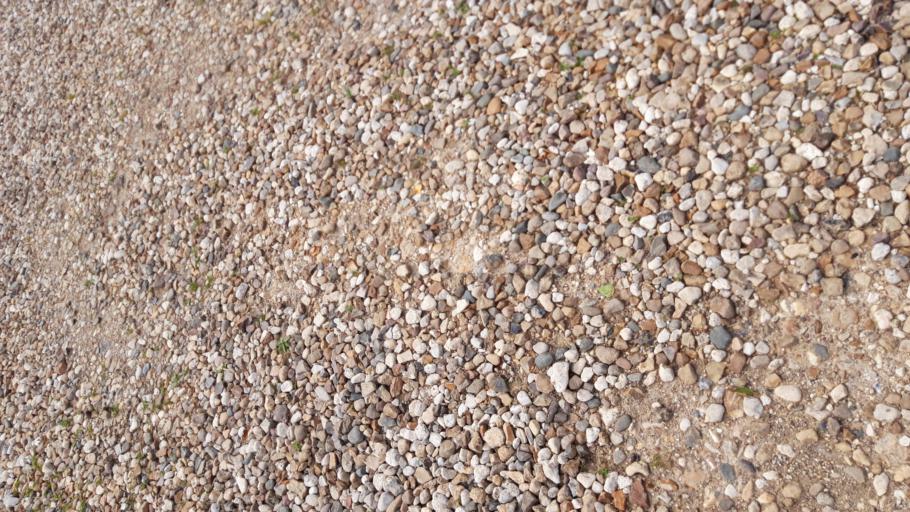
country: RU
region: Tverskaya
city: Konakovo
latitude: 56.6701
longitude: 36.7070
